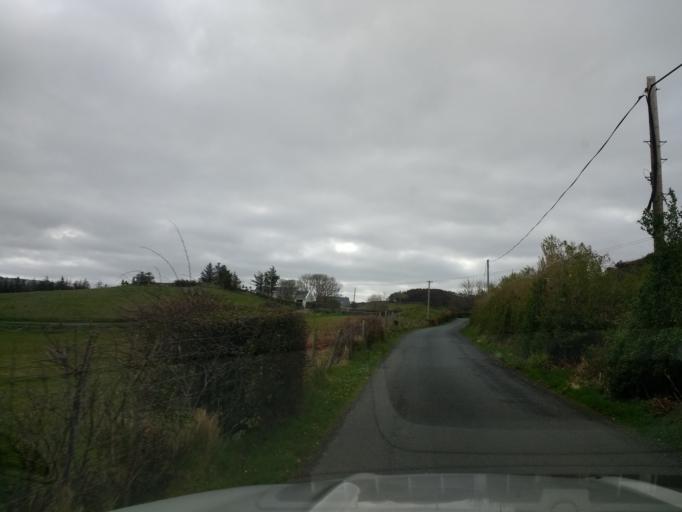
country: IE
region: Ulster
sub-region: County Donegal
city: Buncrana
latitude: 55.2400
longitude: -7.6198
